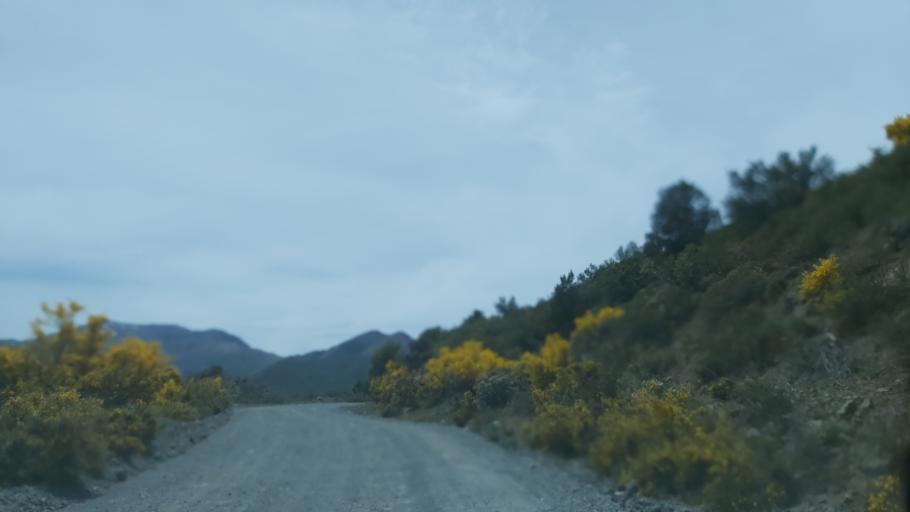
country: AR
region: Neuquen
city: Andacollo
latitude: -37.3927
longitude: -71.4051
